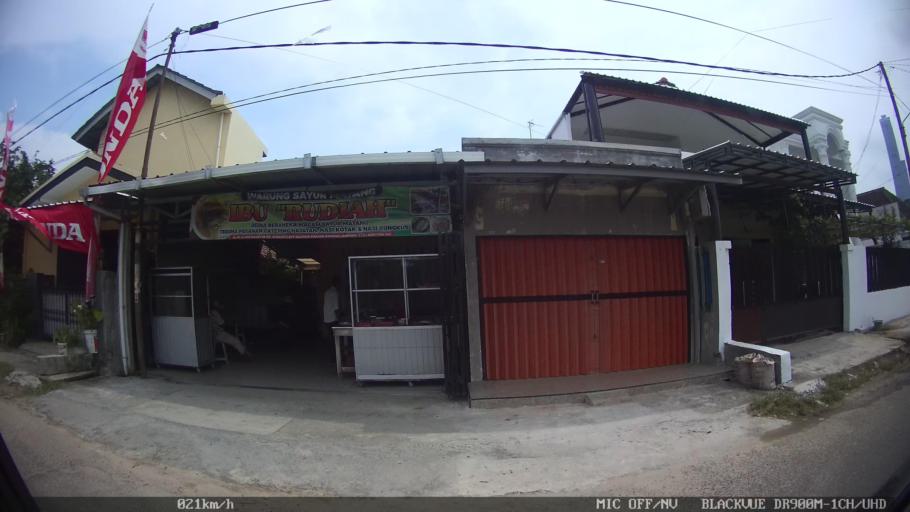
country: ID
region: Lampung
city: Bandarlampung
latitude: -5.4175
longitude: 105.2636
